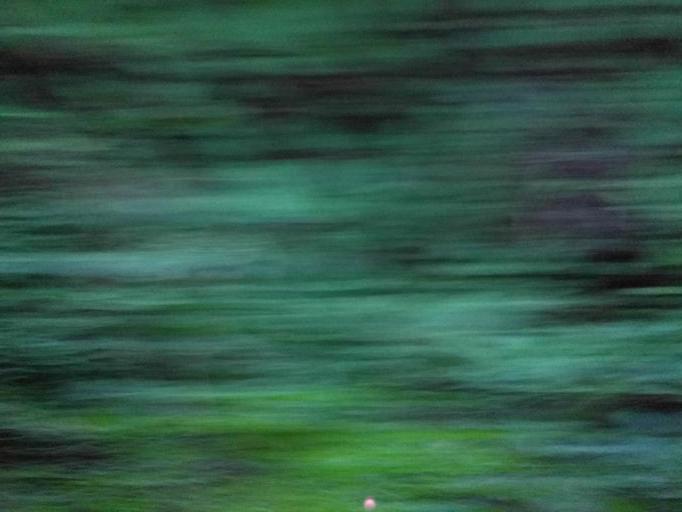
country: JP
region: Fukushima
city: Kitakata
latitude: 37.3633
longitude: 139.8028
